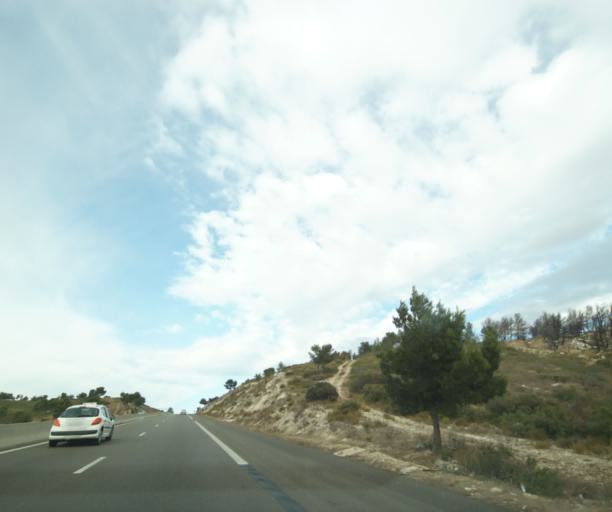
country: FR
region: Provence-Alpes-Cote d'Azur
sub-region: Departement des Bouches-du-Rhone
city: Carry-le-Rouet
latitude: 43.3466
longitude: 5.1698
